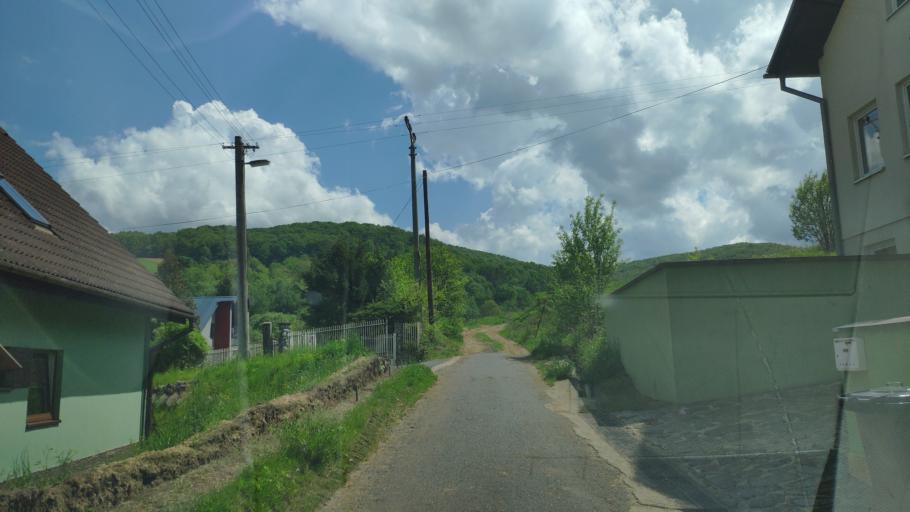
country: SK
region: Presovsky
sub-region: Okres Presov
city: Presov
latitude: 48.9516
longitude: 21.1147
